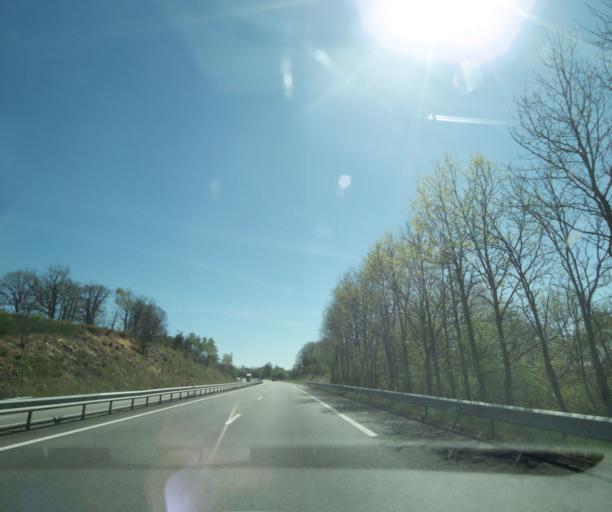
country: FR
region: Limousin
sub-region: Departement de la Haute-Vienne
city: Saint-Germain-les-Belles
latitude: 45.5666
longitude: 1.4970
